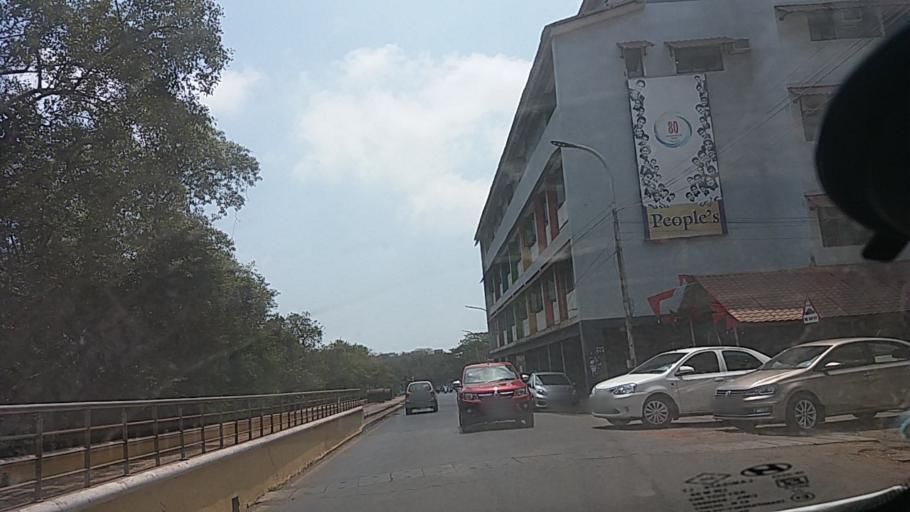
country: IN
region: Goa
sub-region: North Goa
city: Panaji
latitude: 15.4950
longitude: 73.8319
